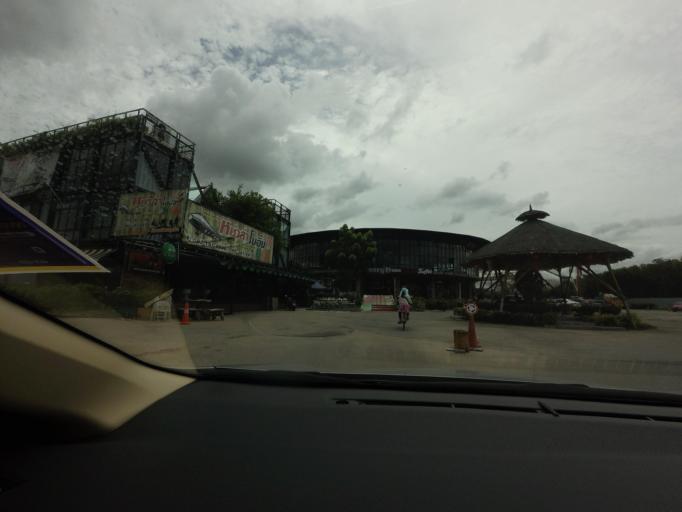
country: TH
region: Bangkok
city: Lat Krabang
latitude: 13.7179
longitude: 100.8018
